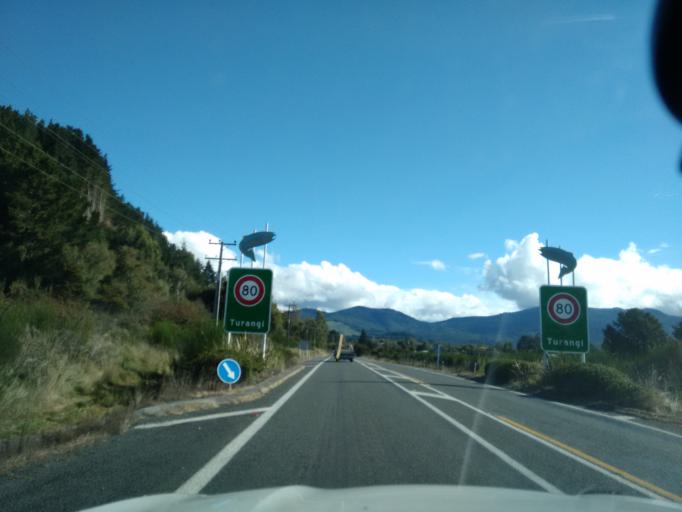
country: NZ
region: Waikato
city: Turangi
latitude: -38.9804
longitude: 175.8255
